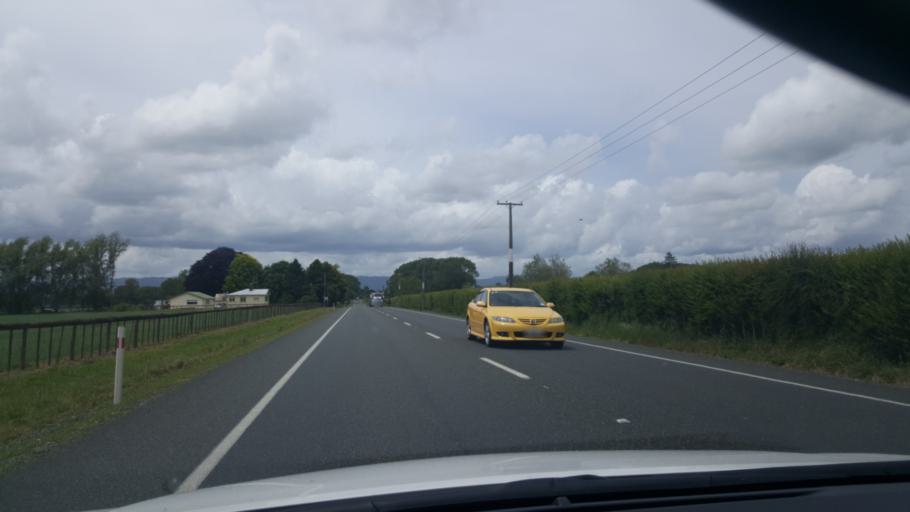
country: NZ
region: Waikato
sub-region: Matamata-Piako District
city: Matamata
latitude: -37.8815
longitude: 175.7422
